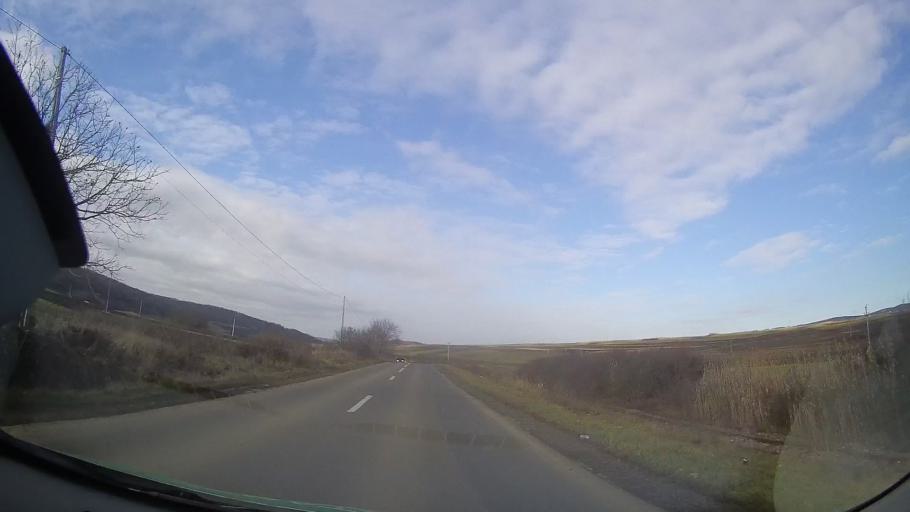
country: RO
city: Barza
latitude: 46.5516
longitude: 24.1135
